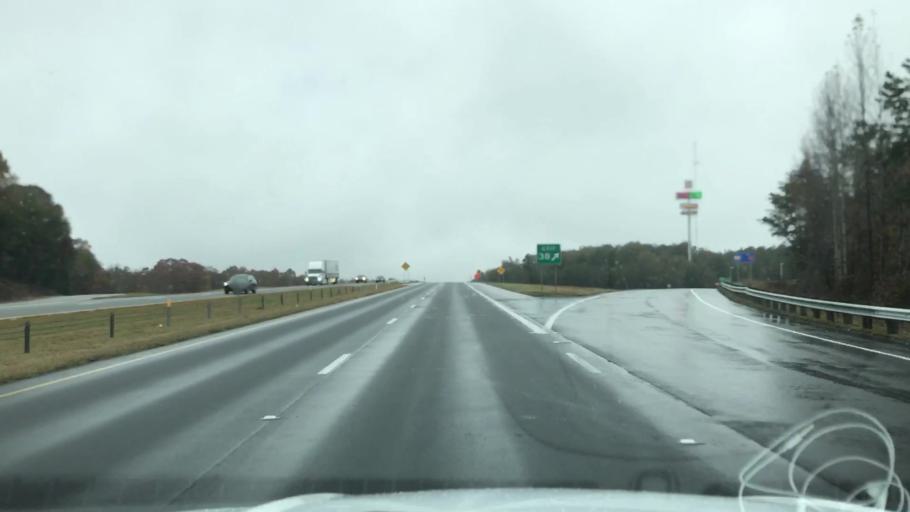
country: US
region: South Carolina
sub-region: Spartanburg County
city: Woodruff
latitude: 34.6959
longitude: -81.9403
